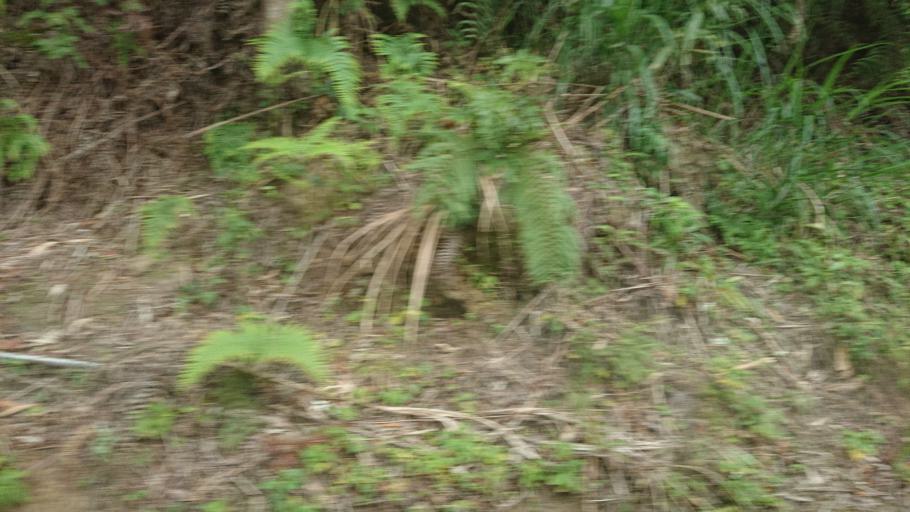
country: TW
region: Taiwan
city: Lugu
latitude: 23.6216
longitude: 120.7203
